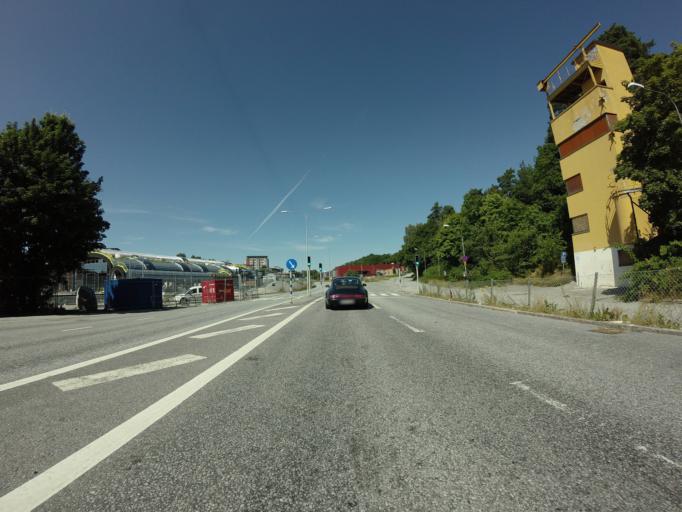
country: SE
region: Stockholm
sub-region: Lidingo
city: Lidingoe
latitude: 59.3470
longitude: 18.1556
